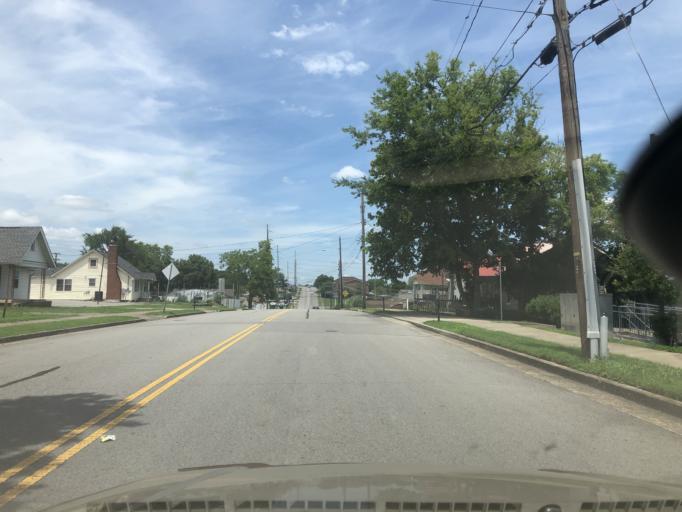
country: US
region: Tennessee
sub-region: Davidson County
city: Goodlettsville
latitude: 36.2590
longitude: -86.7161
